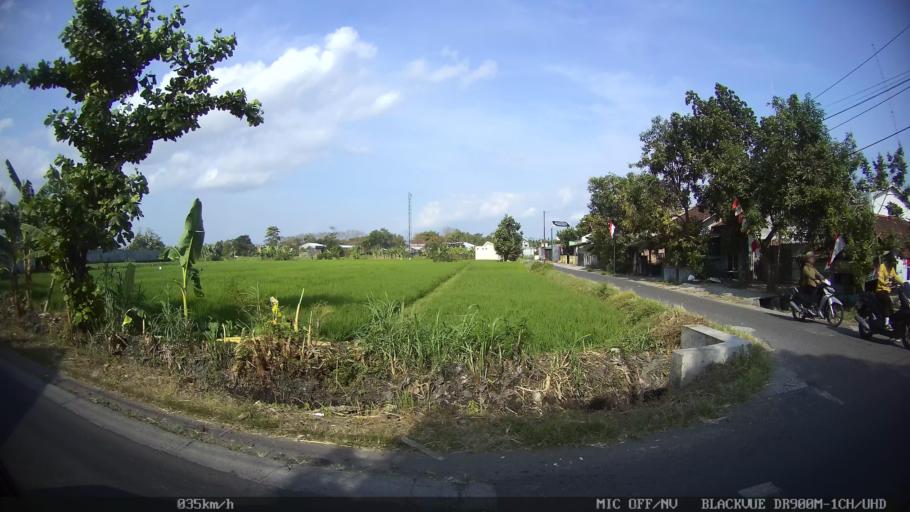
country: ID
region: Daerah Istimewa Yogyakarta
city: Kasihan
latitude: -7.8420
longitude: 110.3439
